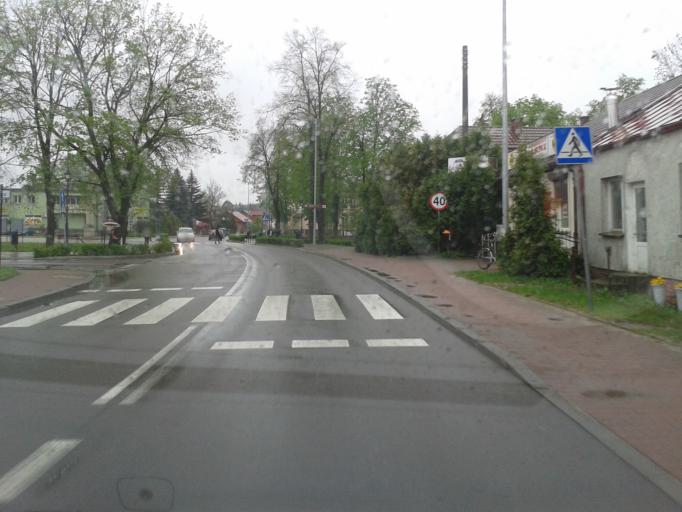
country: PL
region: Subcarpathian Voivodeship
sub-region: Powiat lubaczowski
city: Narol
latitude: 50.3495
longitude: 23.3268
